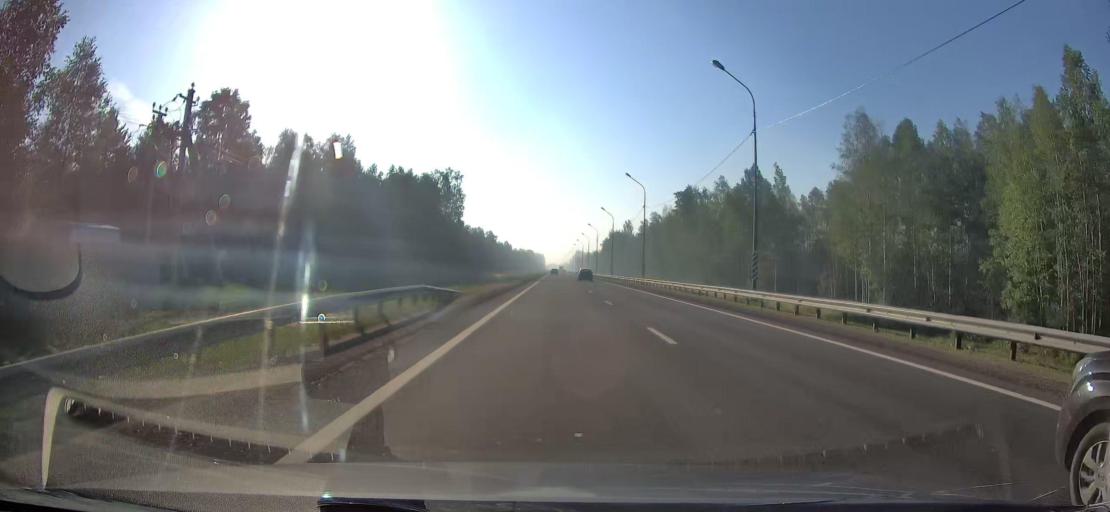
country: RU
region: Leningrad
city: Sinyavino
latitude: 59.8939
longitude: 31.1346
